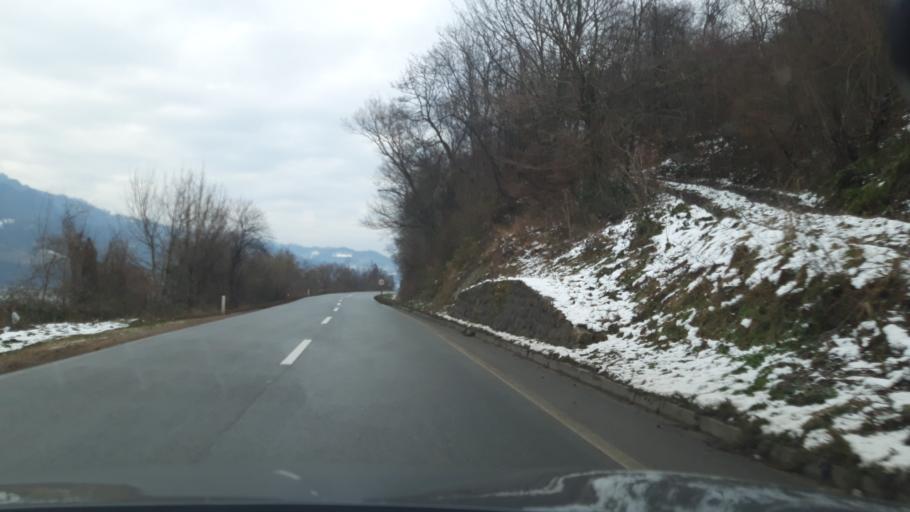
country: RS
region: Central Serbia
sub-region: Macvanski Okrug
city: Mali Zvornik
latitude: 44.3033
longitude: 19.1434
